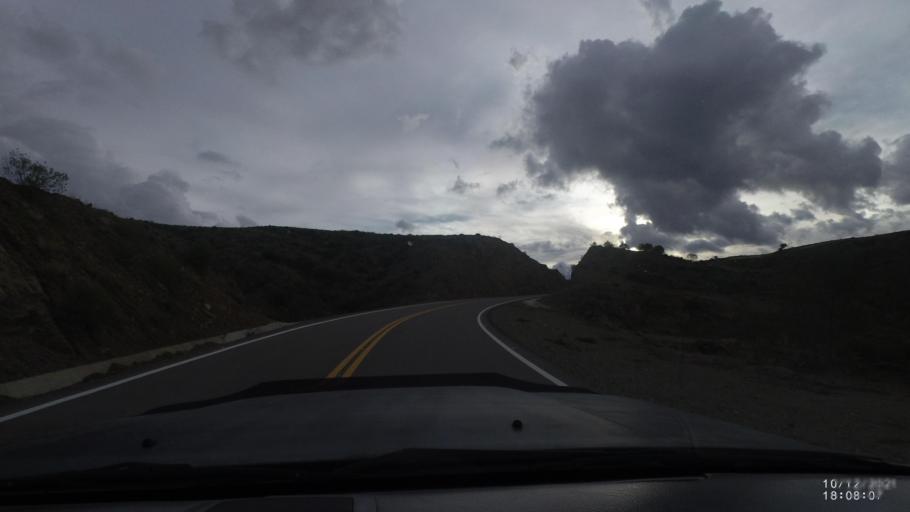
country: BO
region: Cochabamba
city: Tarata
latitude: -17.7903
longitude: -65.9437
